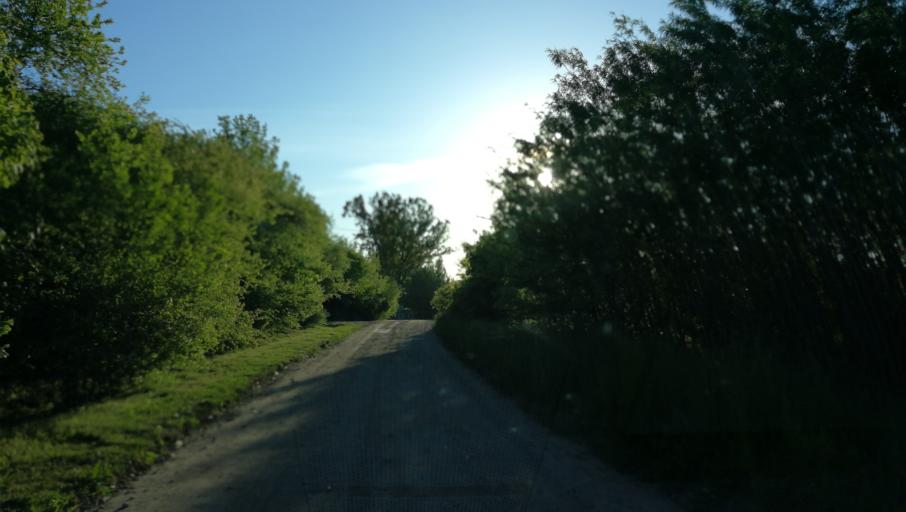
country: LV
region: Dobeles Rajons
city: Dobele
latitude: 56.6200
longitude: 23.2967
